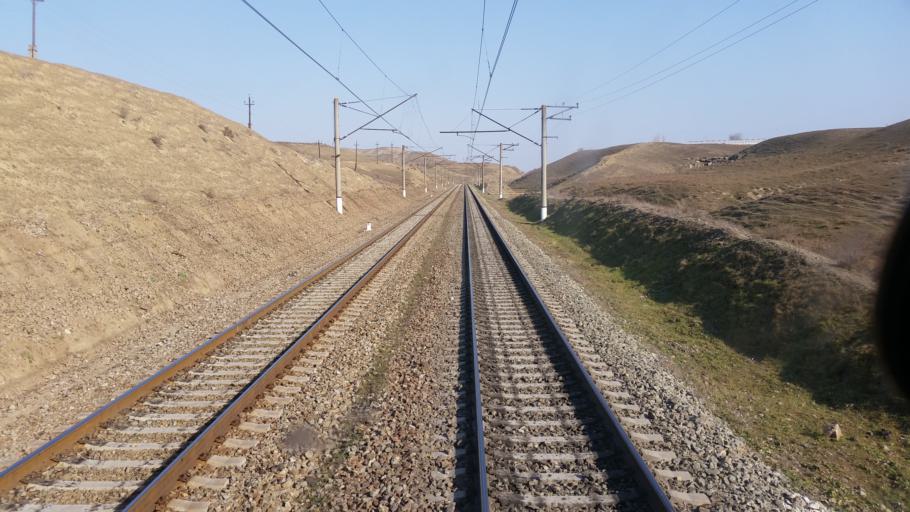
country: AZ
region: Haciqabul
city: Haciqabul
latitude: 40.0446
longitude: 48.9581
